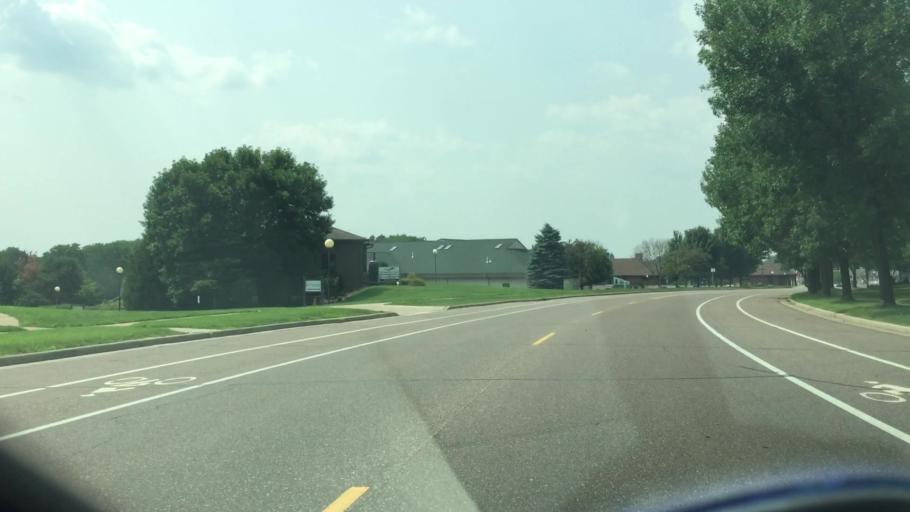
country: US
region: Wisconsin
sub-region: Eau Claire County
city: Altoona
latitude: 44.7689
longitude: -91.4544
